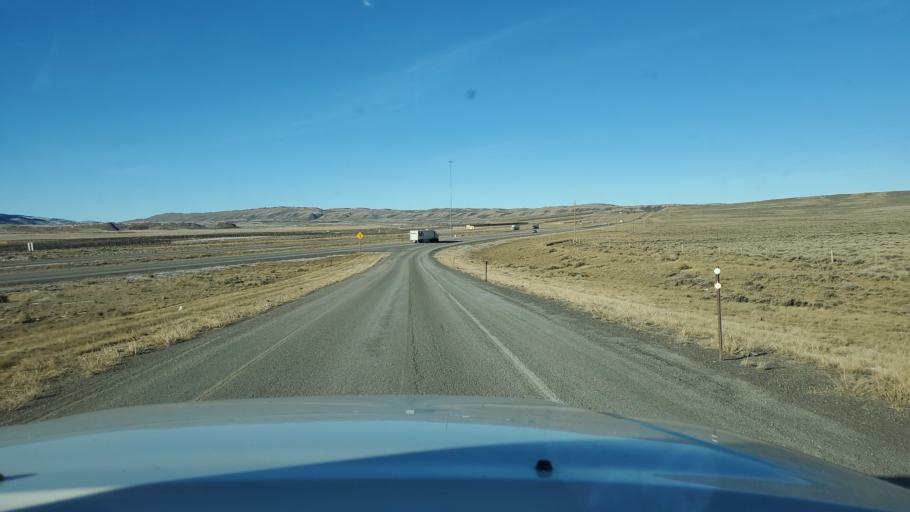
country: US
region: Wyoming
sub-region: Carbon County
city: Saratoga
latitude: 41.7259
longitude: -106.4616
